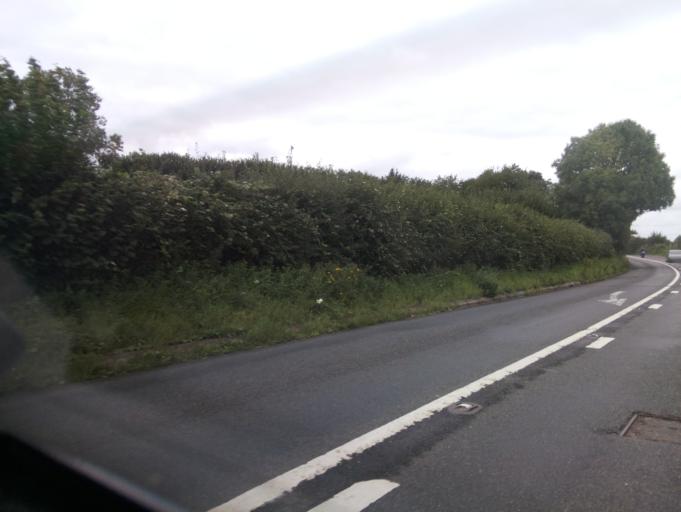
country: GB
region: England
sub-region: Devon
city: Cullompton
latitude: 50.8735
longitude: -3.3869
